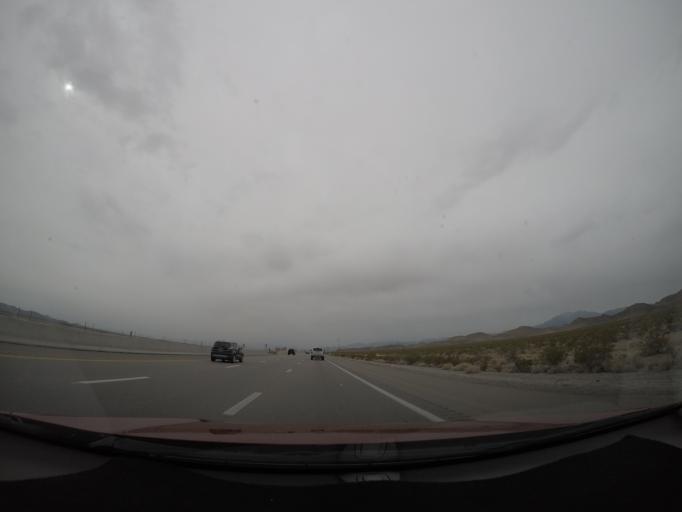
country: US
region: Nevada
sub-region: Clark County
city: Sandy Valley
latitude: 35.6418
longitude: -115.3836
